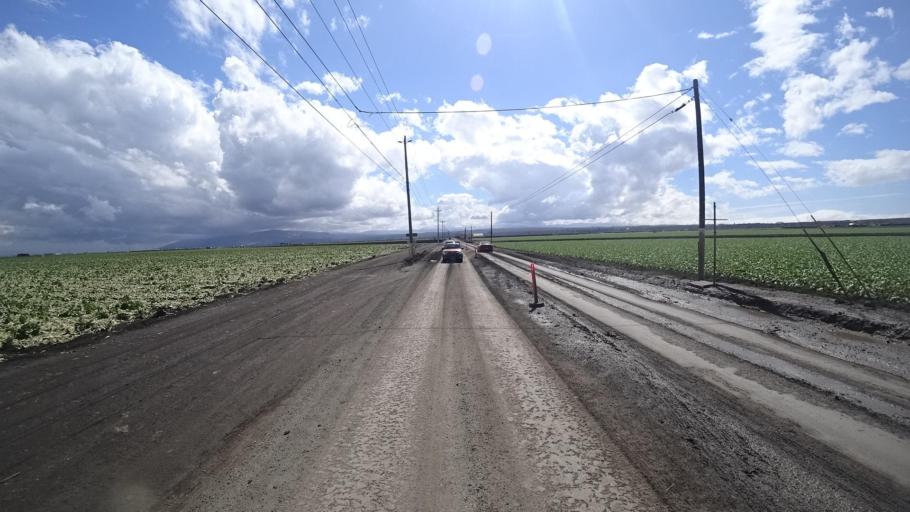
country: US
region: California
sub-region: Monterey County
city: Boronda
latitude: 36.7001
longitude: -121.7350
